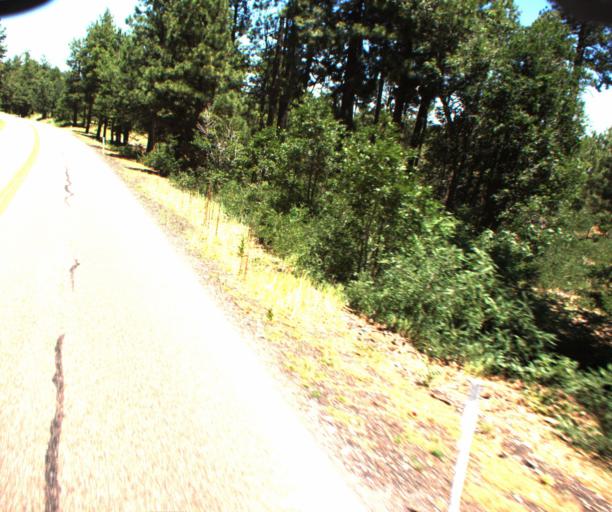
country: US
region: Arizona
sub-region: Gila County
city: Pine
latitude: 34.4723
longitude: -111.3811
